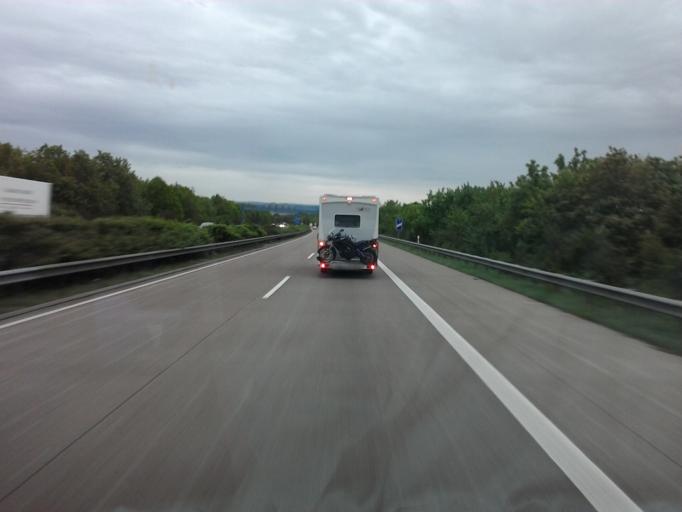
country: DE
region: Rheinland-Pfalz
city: Mendig
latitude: 50.3870
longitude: 7.2626
